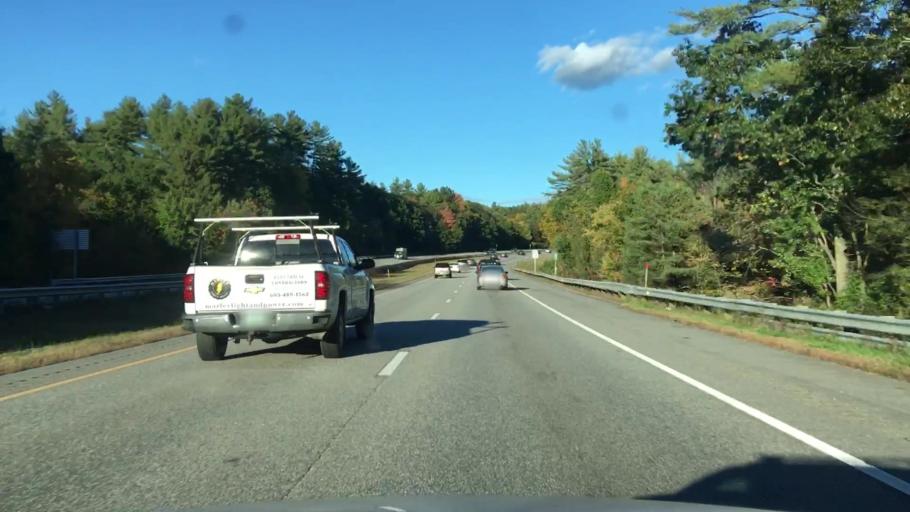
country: US
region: New Hampshire
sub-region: Rockingham County
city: Auburn
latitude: 43.0283
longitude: -71.3588
